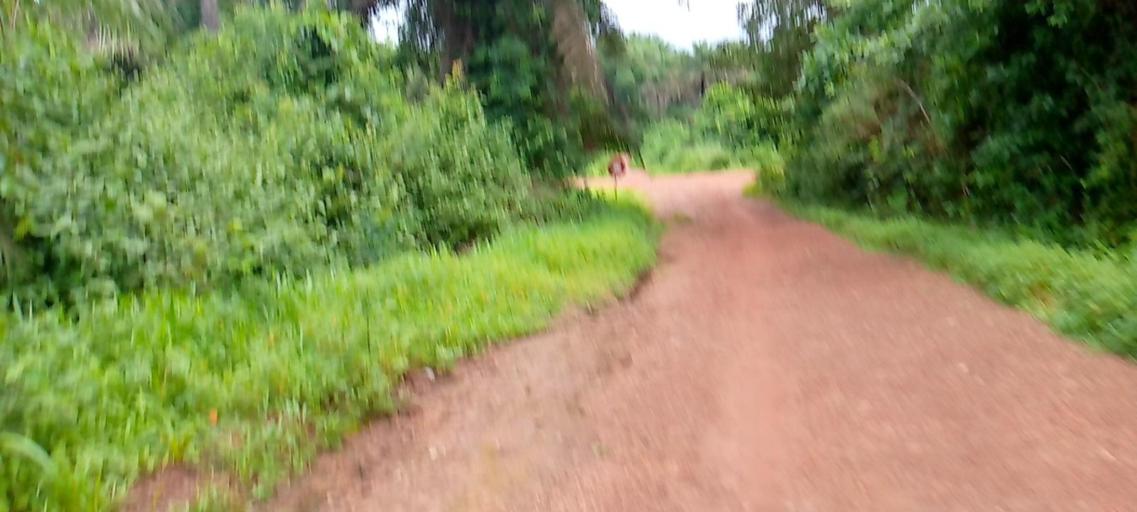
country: SL
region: Northern Province
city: Port Loko
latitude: 8.7213
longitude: -12.8015
